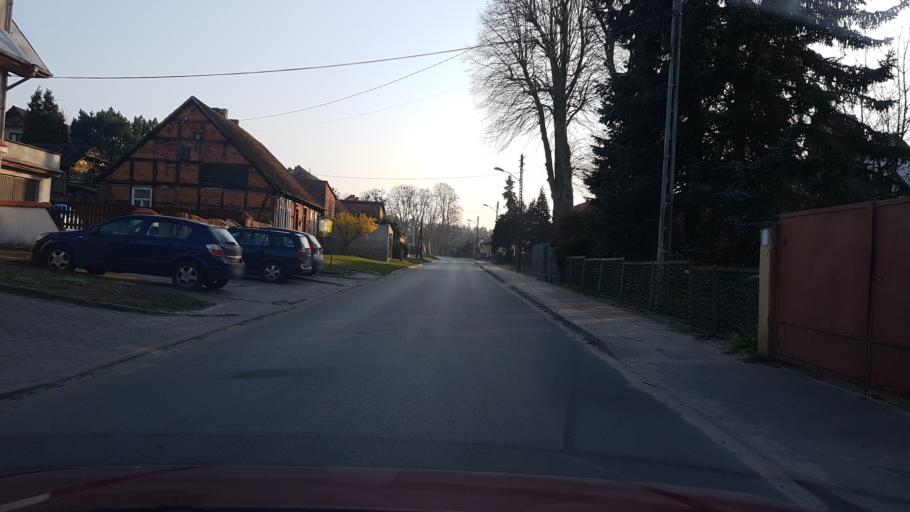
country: PL
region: West Pomeranian Voivodeship
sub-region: Powiat gryfinski
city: Stare Czarnowo
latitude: 53.3418
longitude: 14.7511
